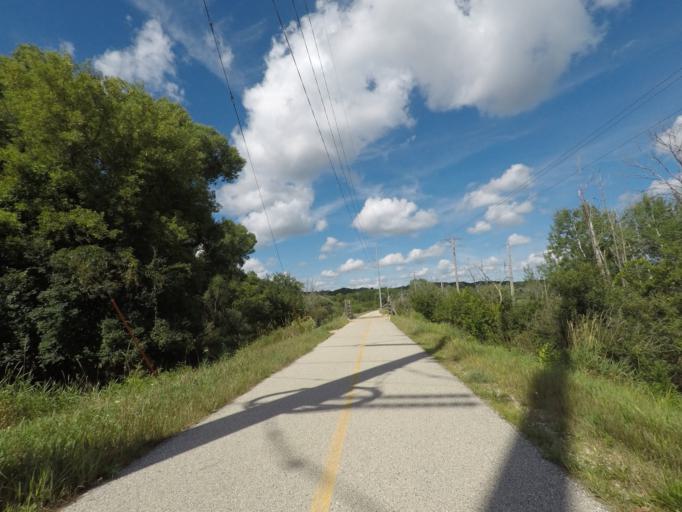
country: US
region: Wisconsin
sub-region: Waukesha County
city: Hartland
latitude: 43.0572
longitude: -88.3442
